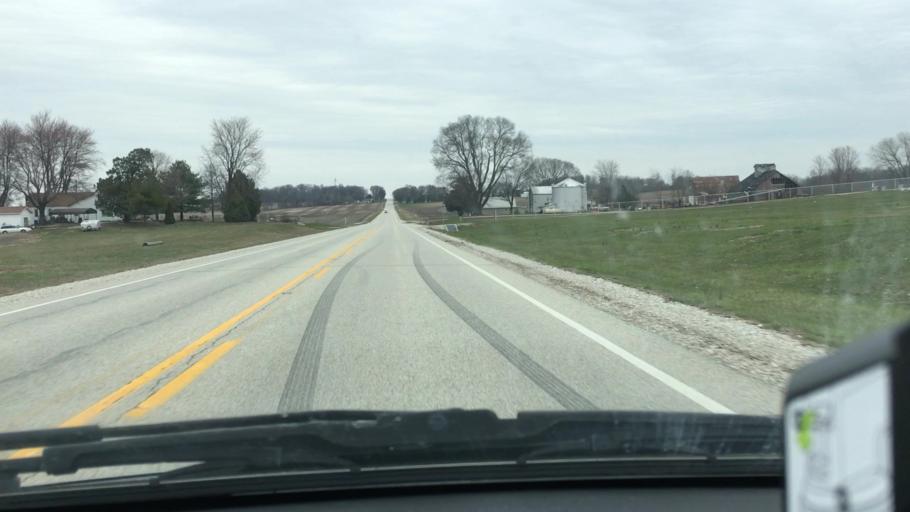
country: US
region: Indiana
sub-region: Greene County
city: Bloomfield
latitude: 38.9791
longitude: -87.0164
